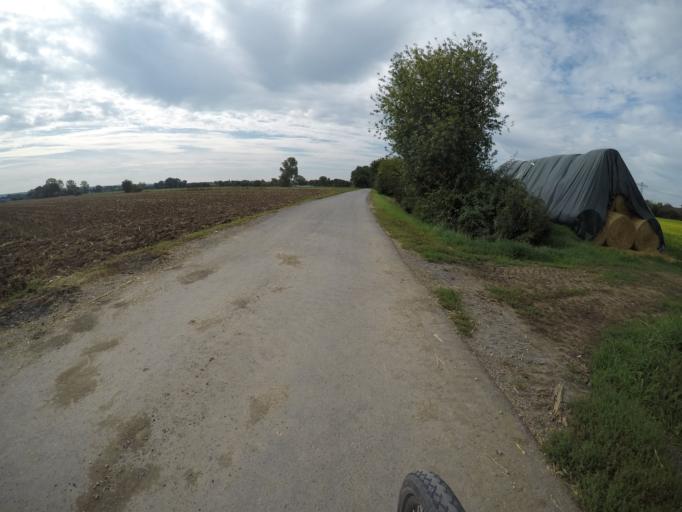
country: DE
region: Baden-Wuerttemberg
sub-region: Karlsruhe Region
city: Kronau
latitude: 49.2353
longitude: 8.6324
